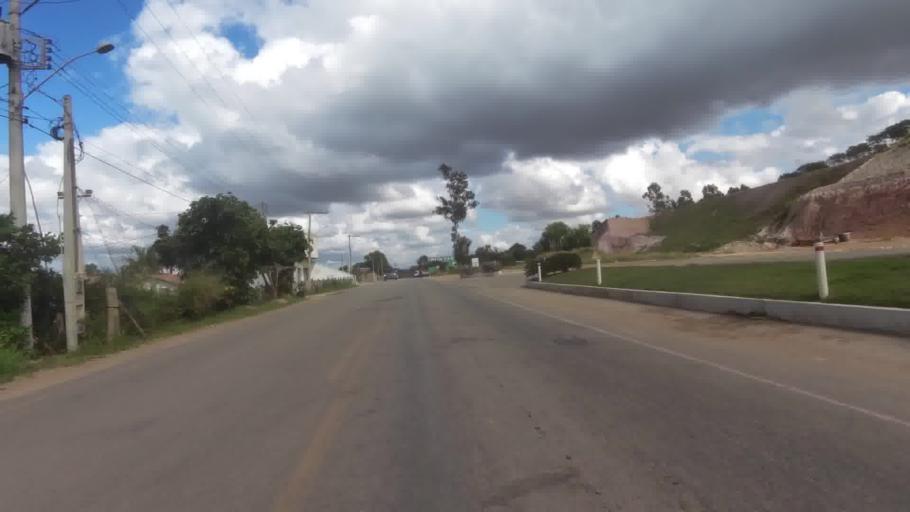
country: BR
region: Espirito Santo
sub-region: Marataizes
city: Marataizes
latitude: -21.2005
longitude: -40.9663
